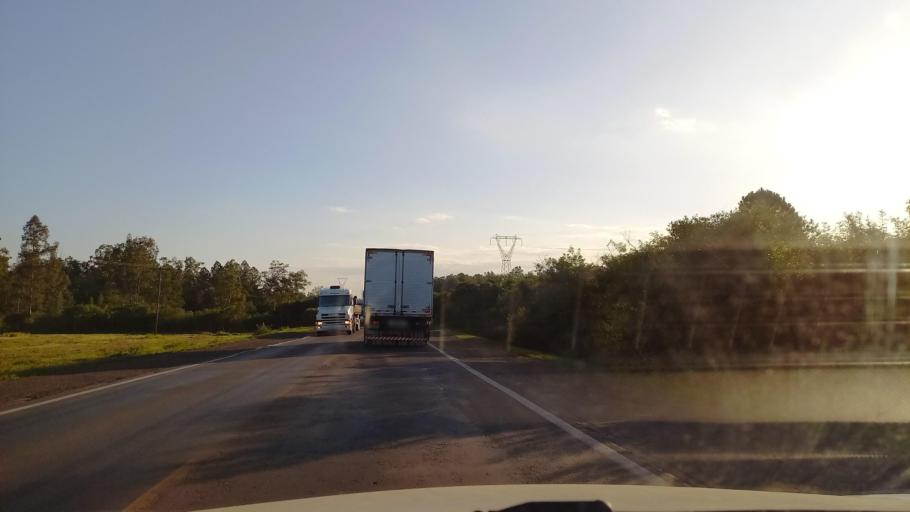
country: BR
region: Rio Grande do Sul
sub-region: Venancio Aires
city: Venancio Aires
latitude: -29.6399
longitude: -52.1637
